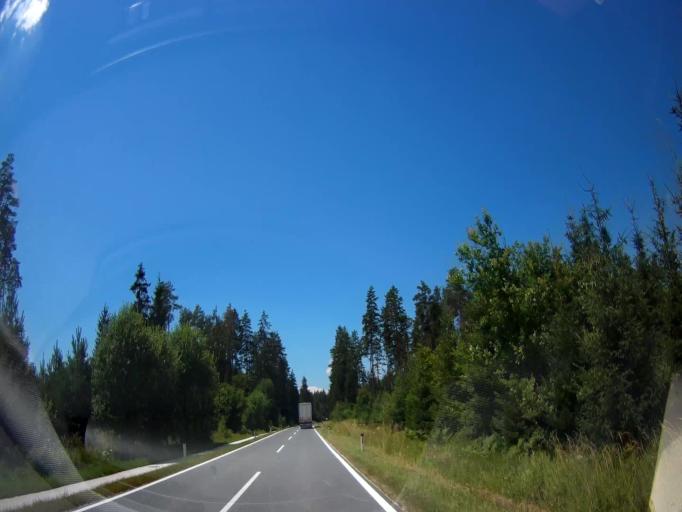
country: AT
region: Carinthia
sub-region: Politischer Bezirk Volkermarkt
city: Eberndorf
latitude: 46.6158
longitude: 14.6602
